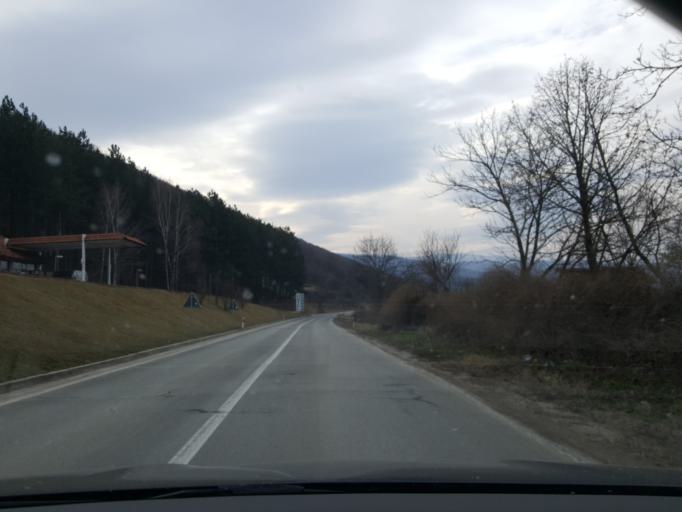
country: RS
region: Central Serbia
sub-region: Pirotski Okrug
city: Dimitrovgrad
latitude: 43.0125
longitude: 22.7768
